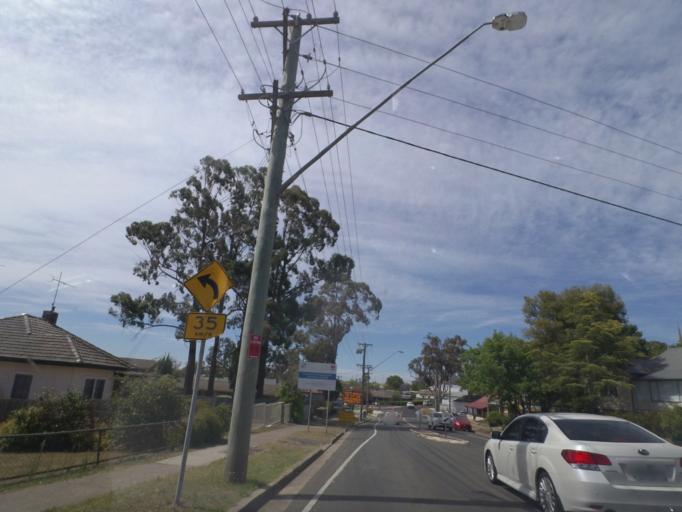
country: AU
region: New South Wales
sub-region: Camden
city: Elderslie
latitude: -34.0582
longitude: 150.6939
